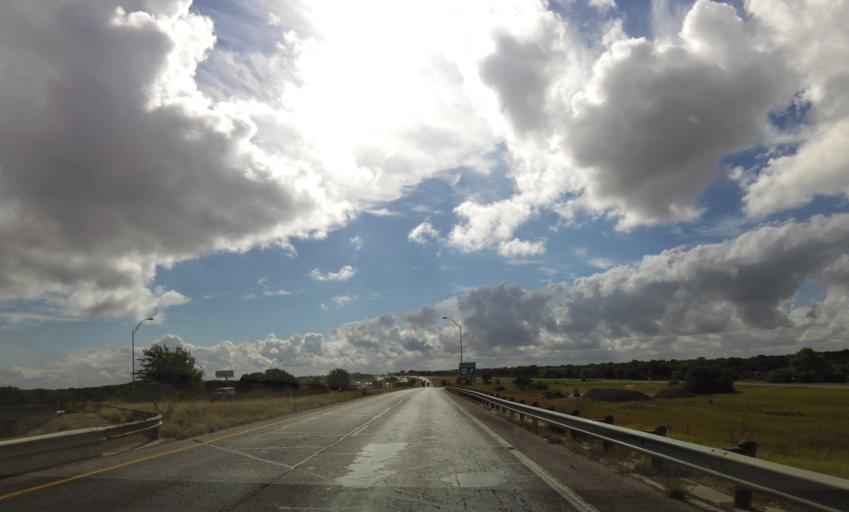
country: US
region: Texas
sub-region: Guadalupe County
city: Seguin
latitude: 29.5993
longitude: -97.9249
